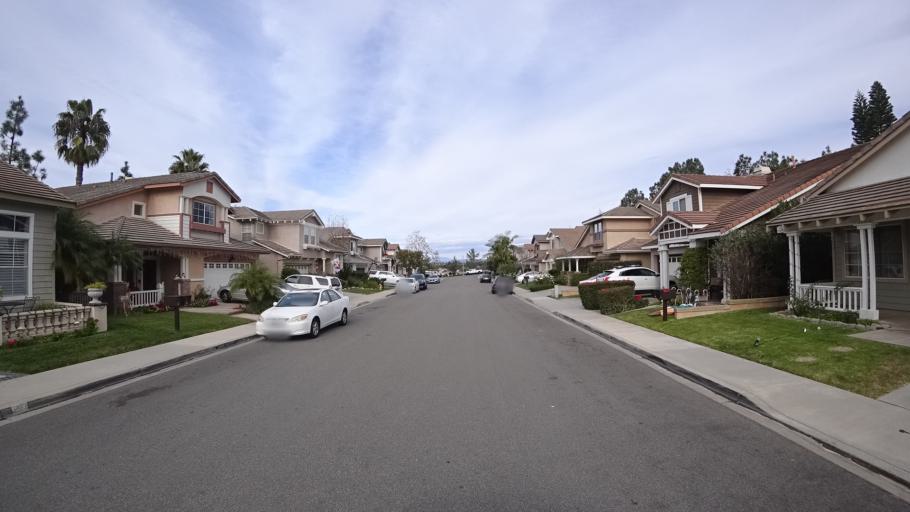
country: US
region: California
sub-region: Orange County
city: Aliso Viejo
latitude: 33.5853
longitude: -117.7396
